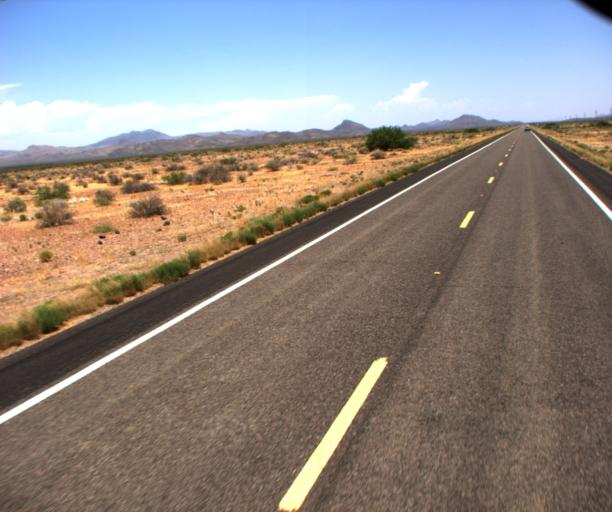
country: US
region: Arizona
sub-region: Graham County
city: Safford
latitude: 32.7744
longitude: -109.4988
